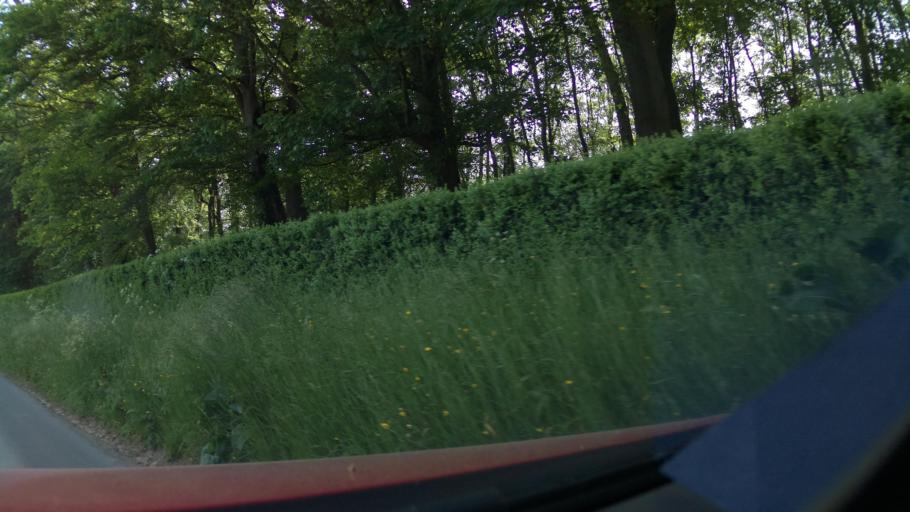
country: GB
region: England
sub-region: Gloucestershire
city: Donnington
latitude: 51.9590
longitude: -1.7657
